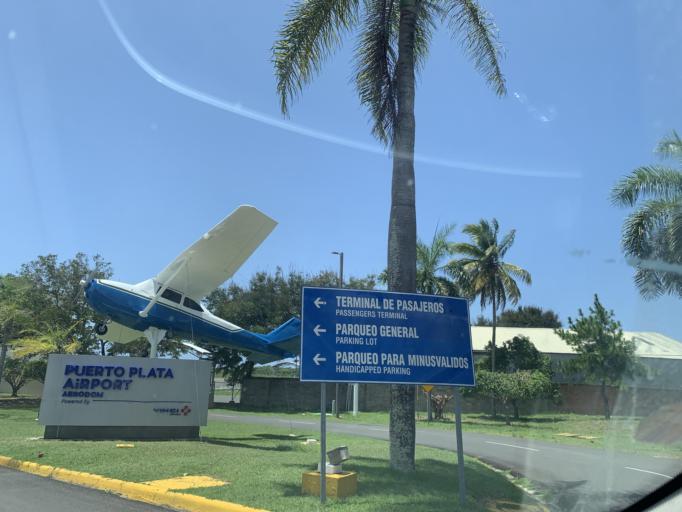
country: DO
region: Puerto Plata
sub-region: Puerto Plata
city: Puerto Plata
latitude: 19.7554
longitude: -70.5619
